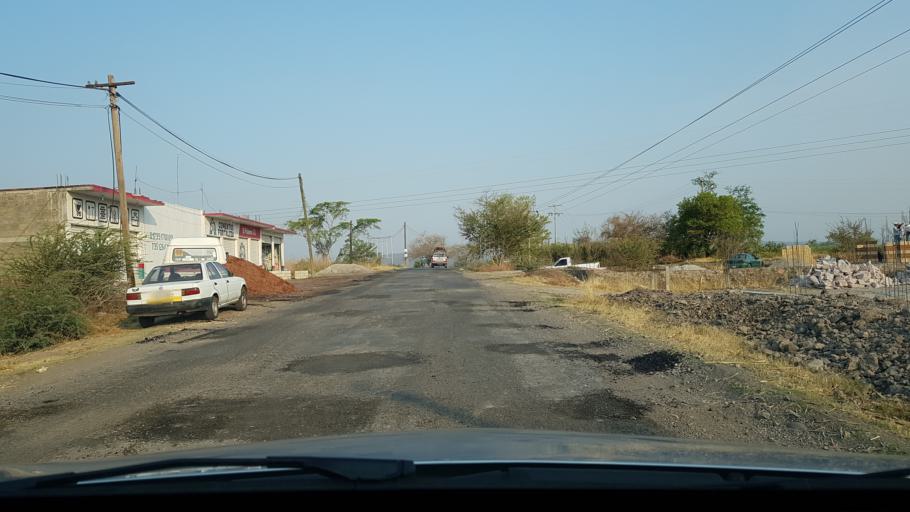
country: MX
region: Morelos
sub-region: Tepalcingo
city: Zacapalco
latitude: 18.6283
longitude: -99.0071
